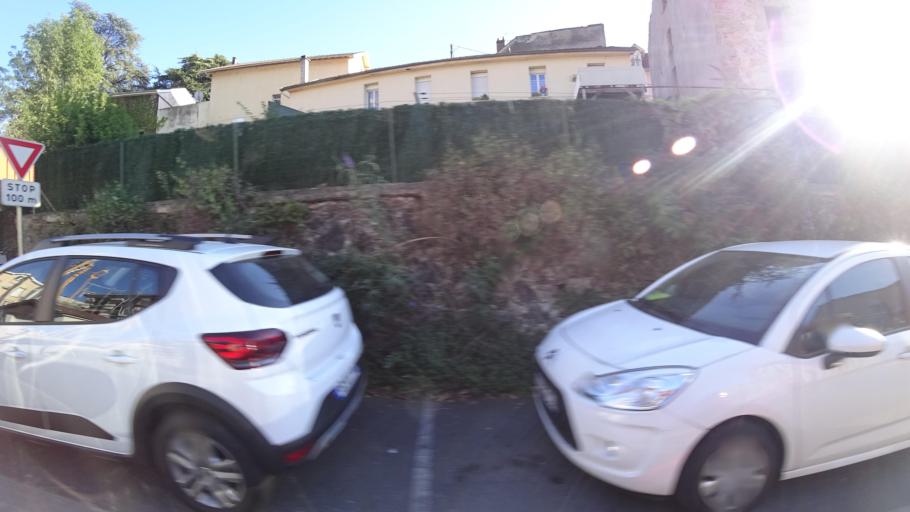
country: FR
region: Midi-Pyrenees
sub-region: Departement de l'Aveyron
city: Cransac
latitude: 44.5249
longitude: 2.2848
